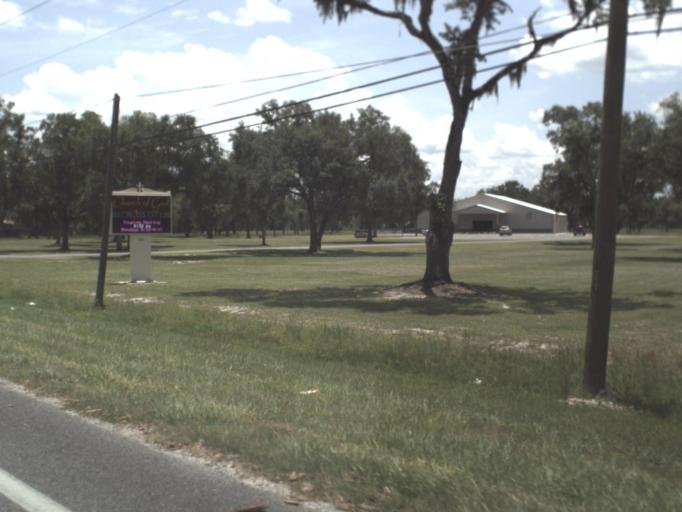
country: US
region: Florida
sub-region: Dixie County
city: Cross City
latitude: 29.6223
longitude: -83.1048
